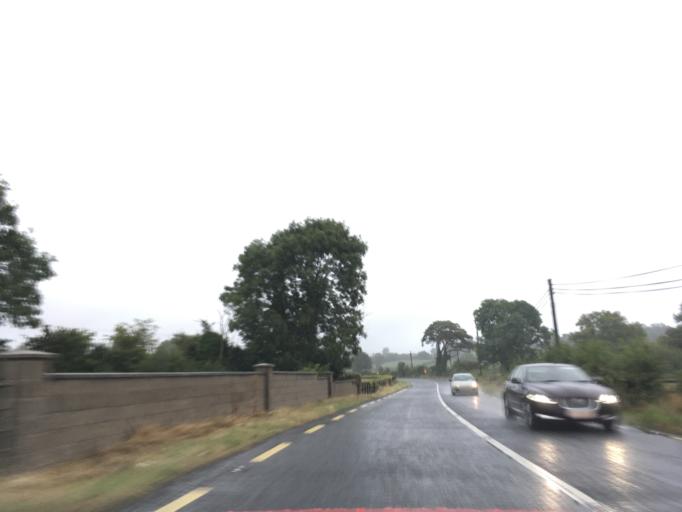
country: IE
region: Munster
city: Tipperary
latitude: 52.4815
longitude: -8.1064
